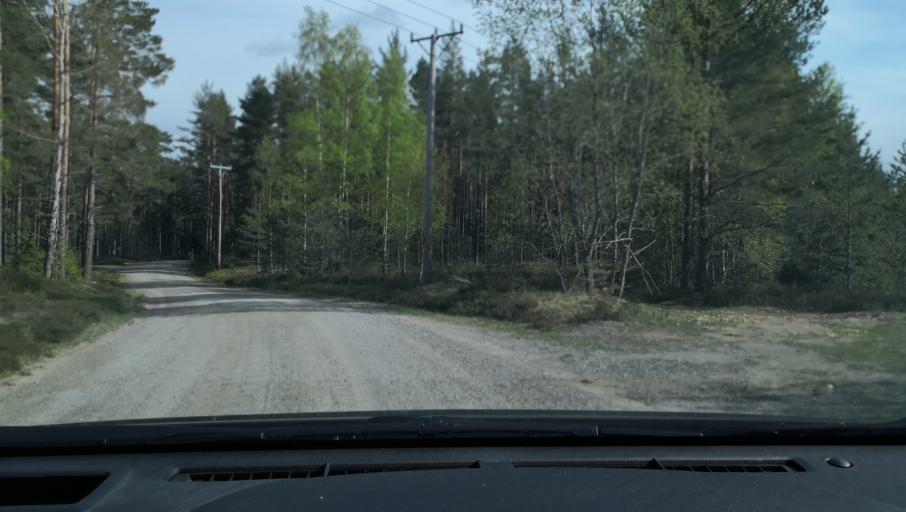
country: SE
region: OErebro
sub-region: Askersunds Kommun
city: Asbro
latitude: 59.0317
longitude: 15.0452
